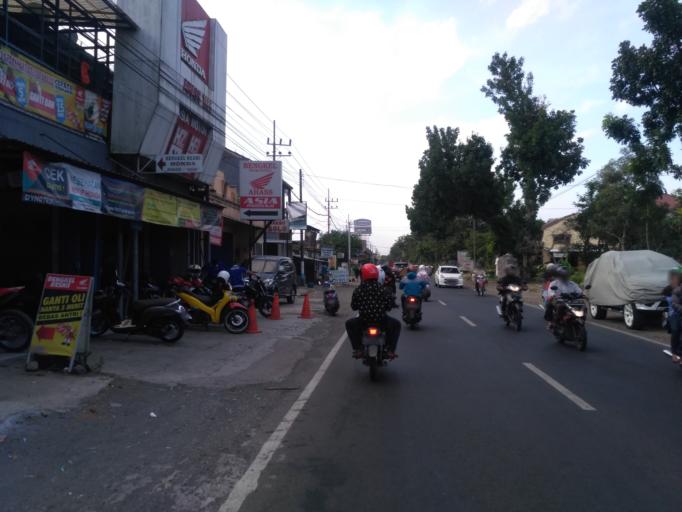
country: ID
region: East Java
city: Pakisaji
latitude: -8.0606
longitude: 112.6013
